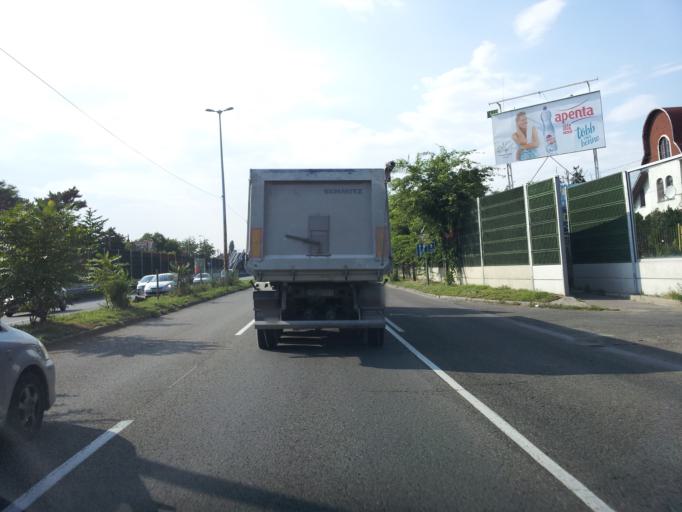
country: HU
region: Budapest
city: Budapest XIX. keruelet
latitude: 47.4427
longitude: 19.1323
